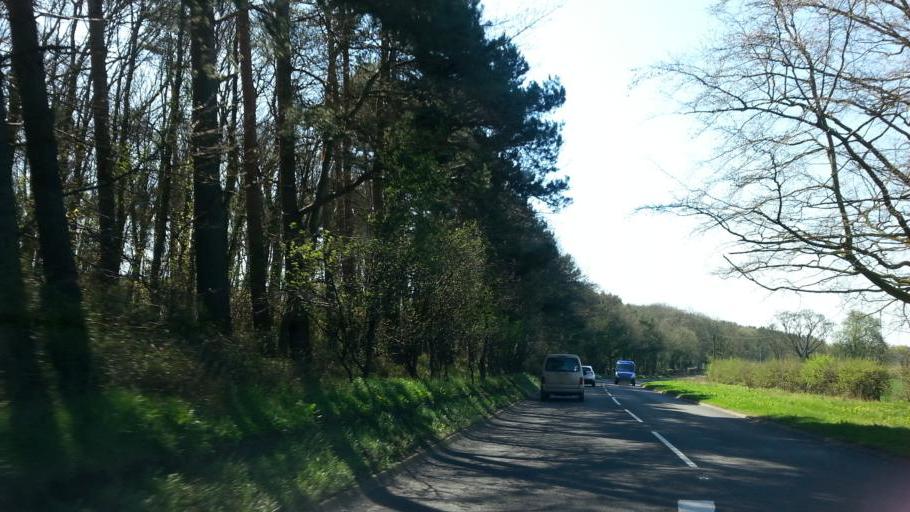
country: GB
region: England
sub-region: Staffordshire
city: Stafford
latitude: 52.8217
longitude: -2.0708
